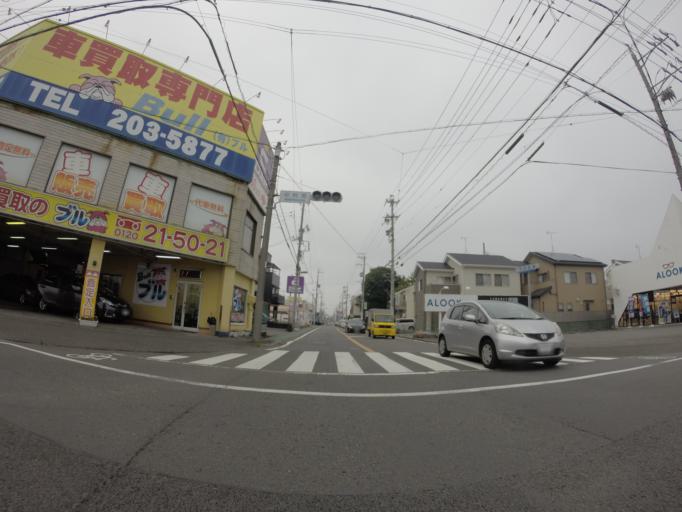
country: JP
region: Shizuoka
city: Shizuoka-shi
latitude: 34.9536
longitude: 138.3939
